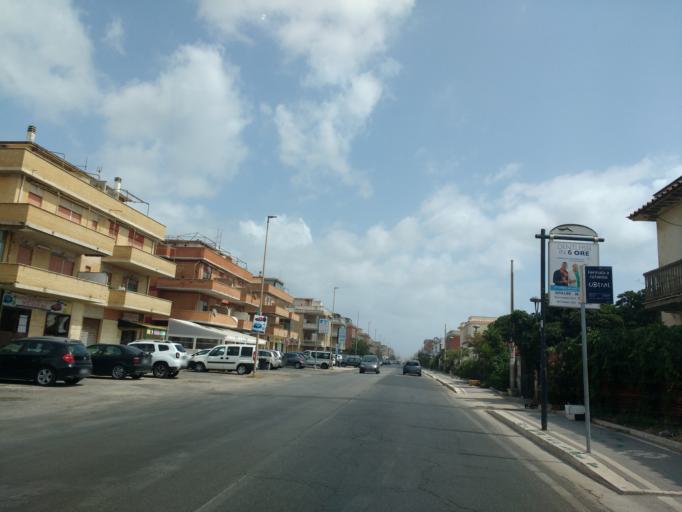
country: IT
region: Latium
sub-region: Citta metropolitana di Roma Capitale
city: Ardea
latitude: 41.5911
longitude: 12.4942
